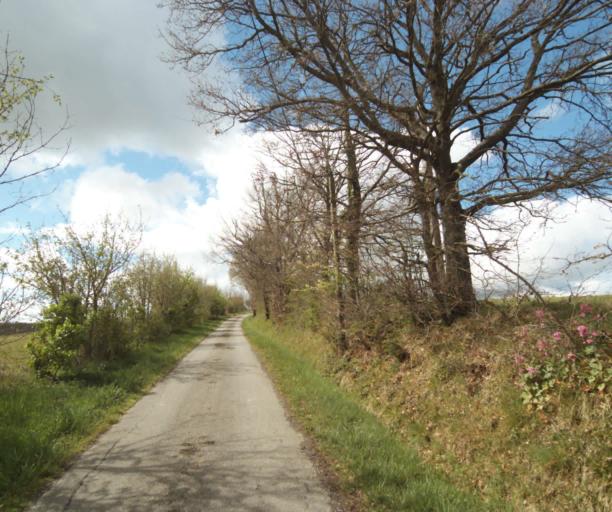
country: FR
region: Midi-Pyrenees
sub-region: Departement de l'Ariege
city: Saverdun
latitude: 43.1975
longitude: 1.5758
